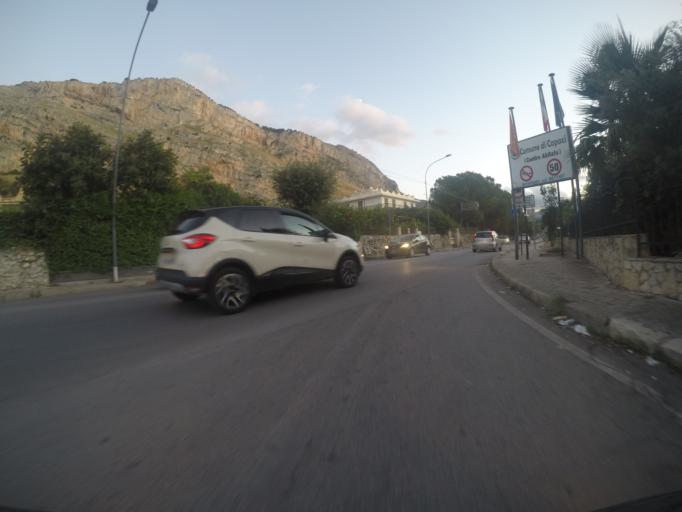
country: IT
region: Sicily
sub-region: Palermo
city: Capaci
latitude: 38.1790
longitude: 13.2442
